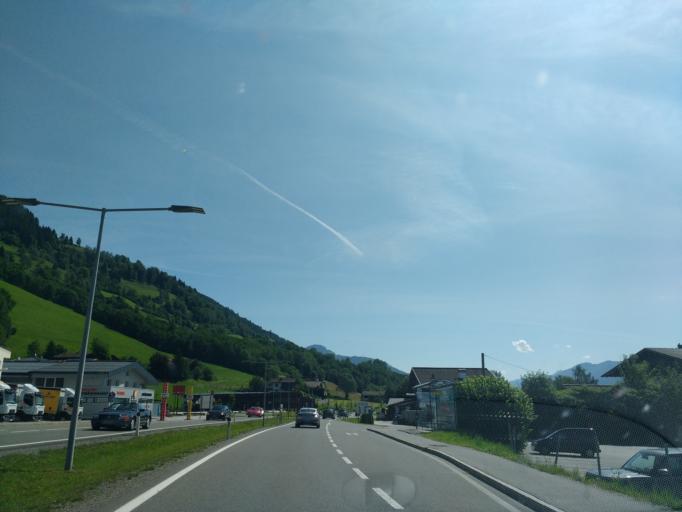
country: AT
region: Salzburg
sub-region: Politischer Bezirk Zell am See
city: Piesendorf
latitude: 47.2917
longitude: 12.7230
